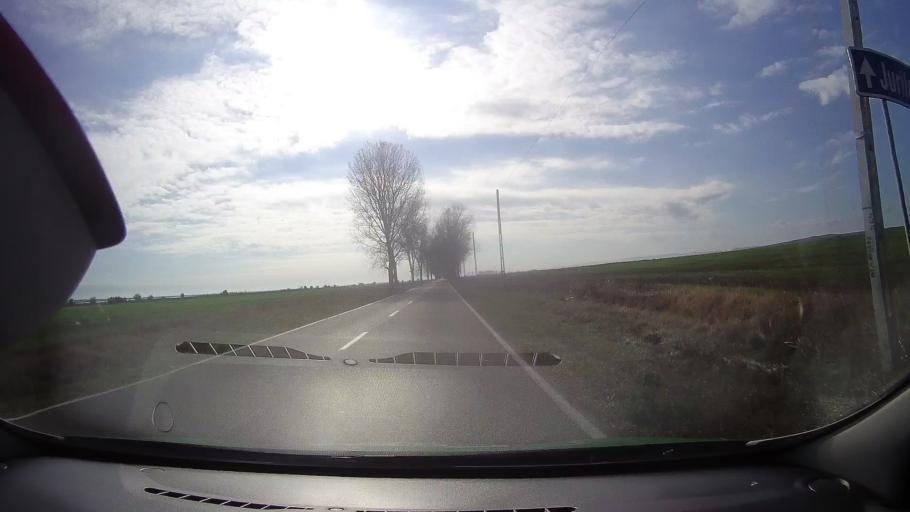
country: RO
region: Tulcea
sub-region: Comuna Valea Nucarilor
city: Agighiol
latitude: 45.0135
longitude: 28.8838
